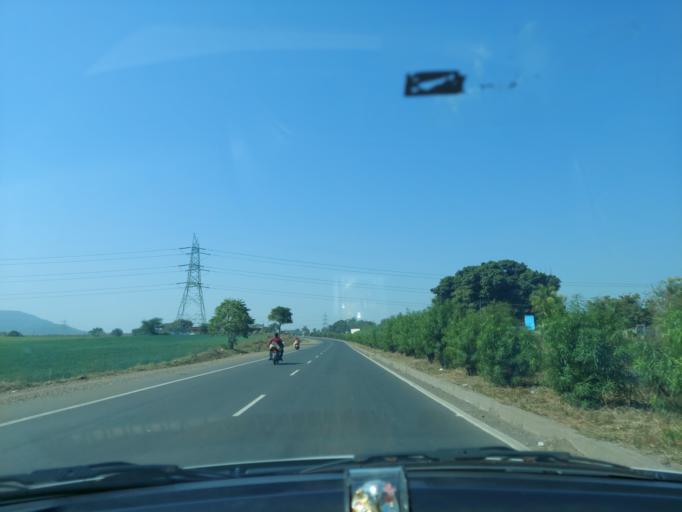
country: IN
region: Madhya Pradesh
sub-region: Indore
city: Manpur
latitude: 22.4225
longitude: 75.6037
